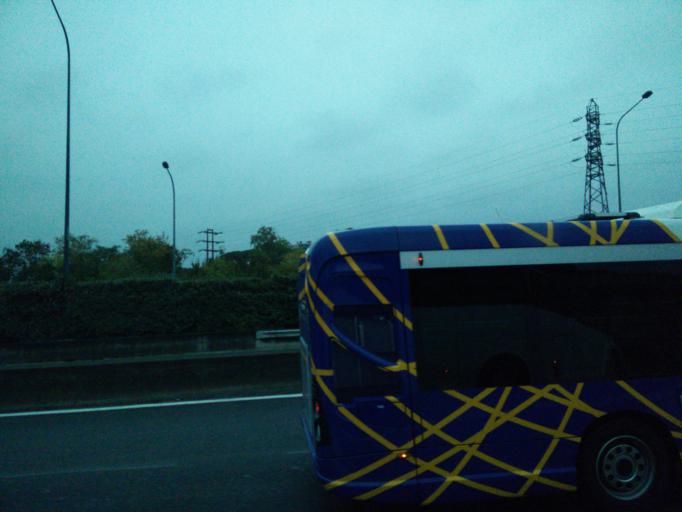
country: FR
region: Midi-Pyrenees
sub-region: Departement de la Haute-Garonne
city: Blagnac
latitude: 43.6194
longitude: 1.3940
